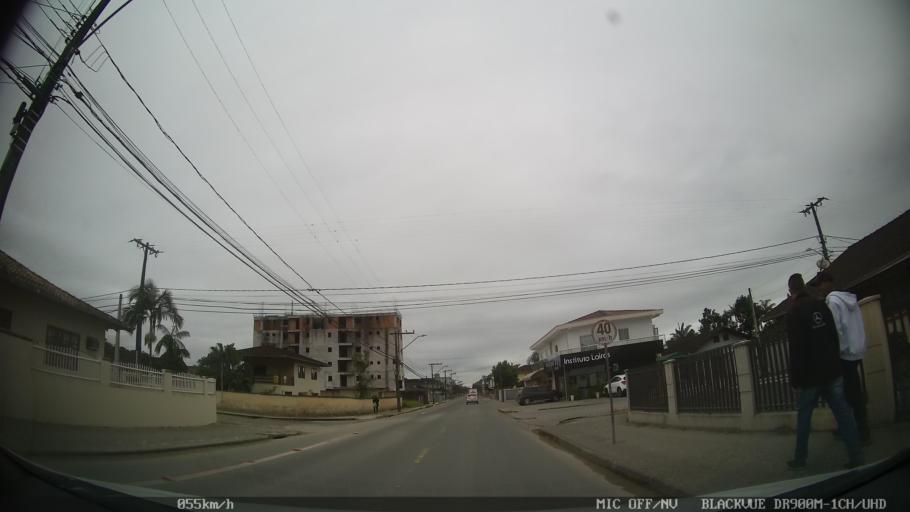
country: BR
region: Santa Catarina
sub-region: Joinville
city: Joinville
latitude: -26.2808
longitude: -48.8989
